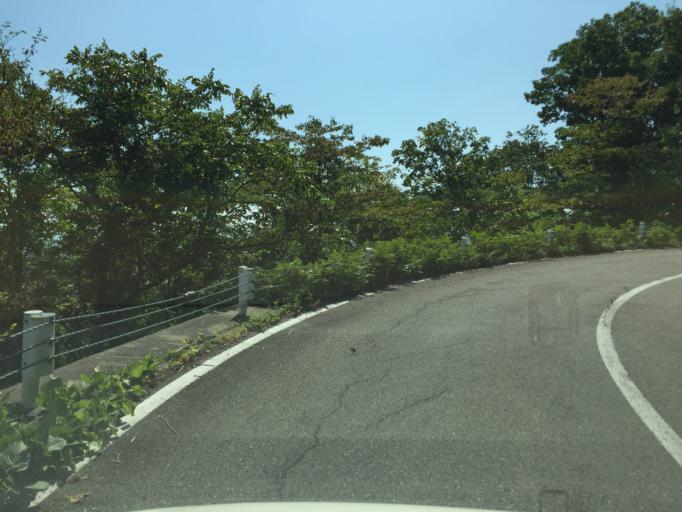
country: JP
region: Fukushima
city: Inawashiro
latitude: 37.5749
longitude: 140.0261
